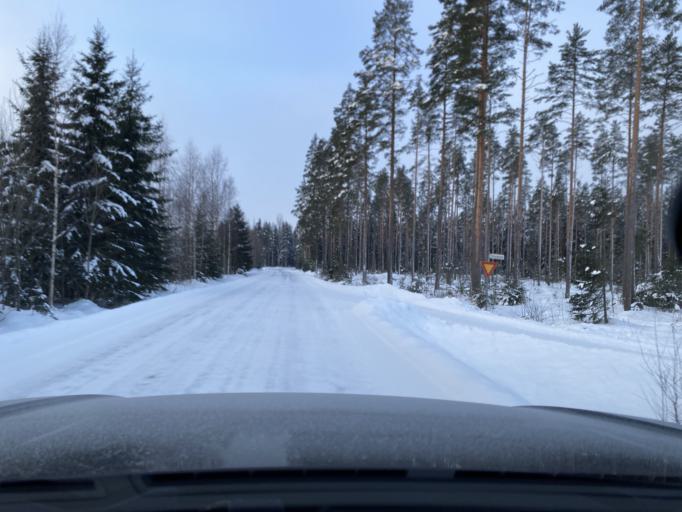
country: FI
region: Haeme
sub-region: Forssa
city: Tammela
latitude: 60.8629
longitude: 23.8725
